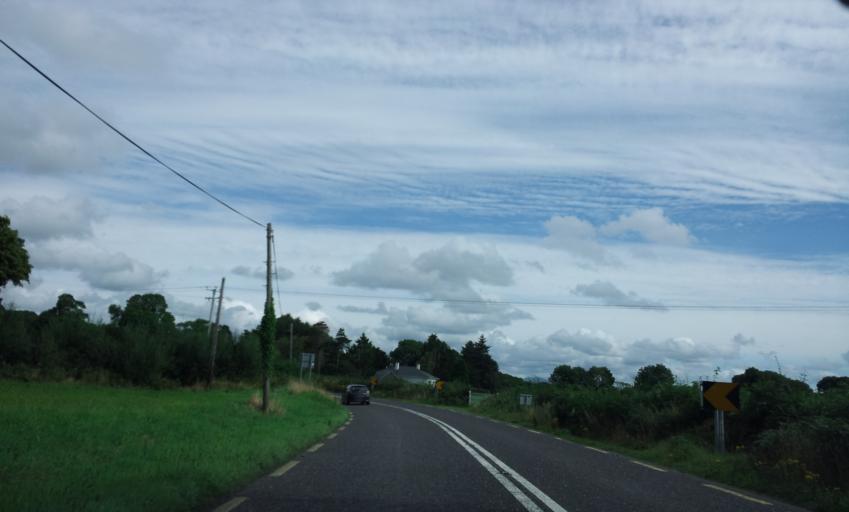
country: IE
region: Munster
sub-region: Ciarrai
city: Cill Airne
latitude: 52.0717
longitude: -9.6033
